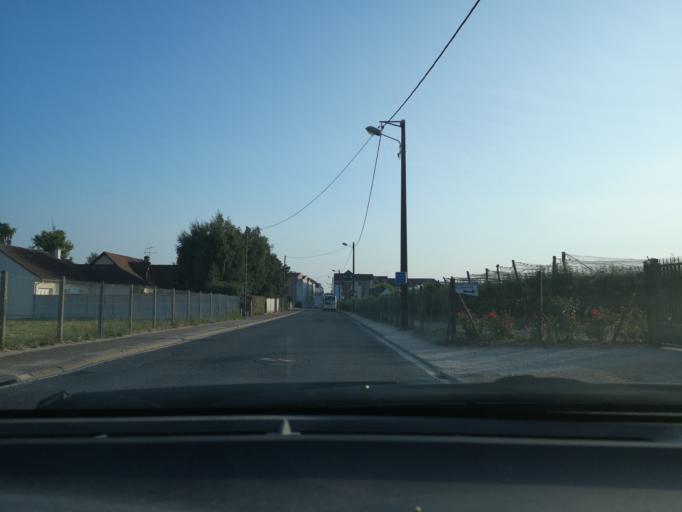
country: FR
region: Centre
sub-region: Departement du Loiret
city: Fleury-les-Aubrais
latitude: 47.9372
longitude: 1.9298
